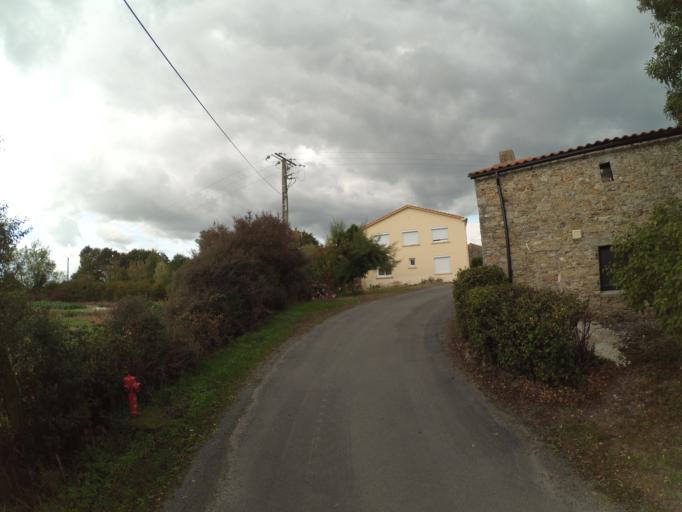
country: FR
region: Pays de la Loire
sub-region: Departement de la Loire-Atlantique
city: Remouille
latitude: 47.0573
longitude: -1.3617
